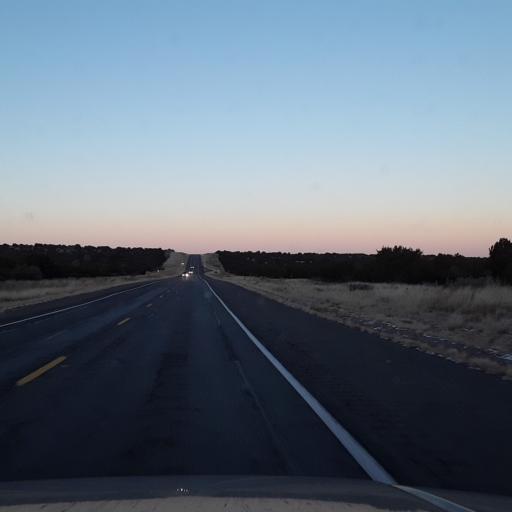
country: US
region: New Mexico
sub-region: Guadalupe County
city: Santa Rosa
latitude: 34.5255
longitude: -105.3267
